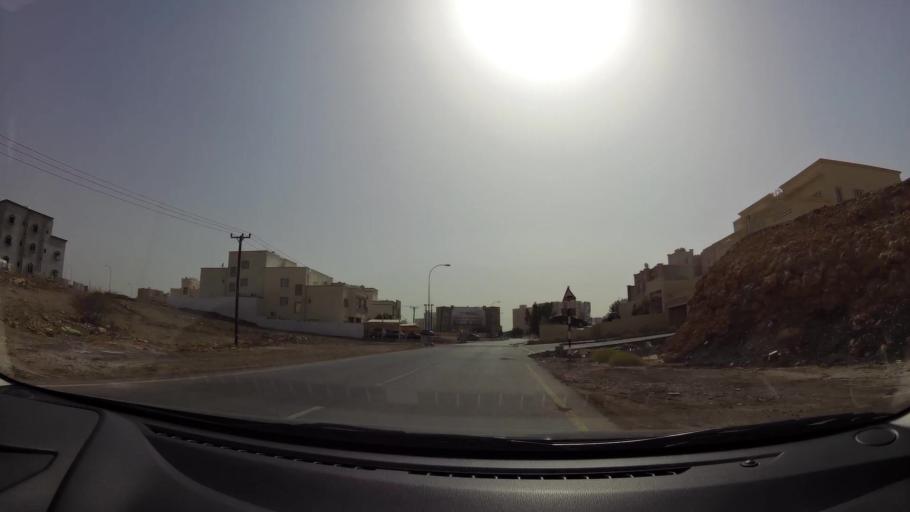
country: OM
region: Muhafazat Masqat
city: Bawshar
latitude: 23.5506
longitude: 58.3502
